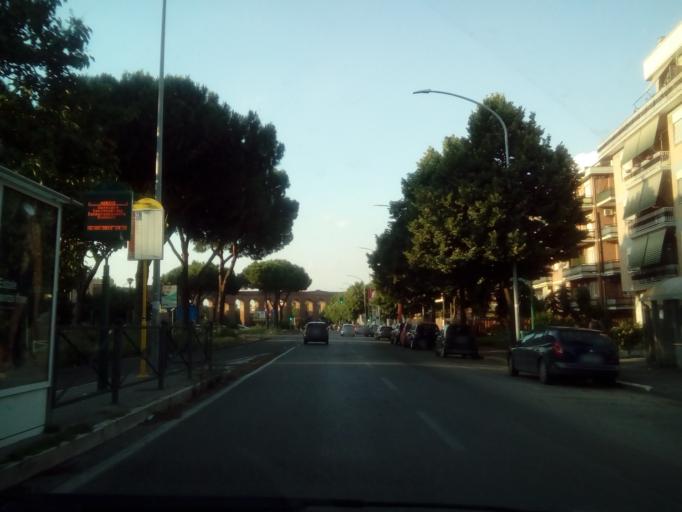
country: IT
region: Latium
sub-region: Citta metropolitana di Roma Capitale
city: Rome
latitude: 41.8763
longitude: 12.5716
